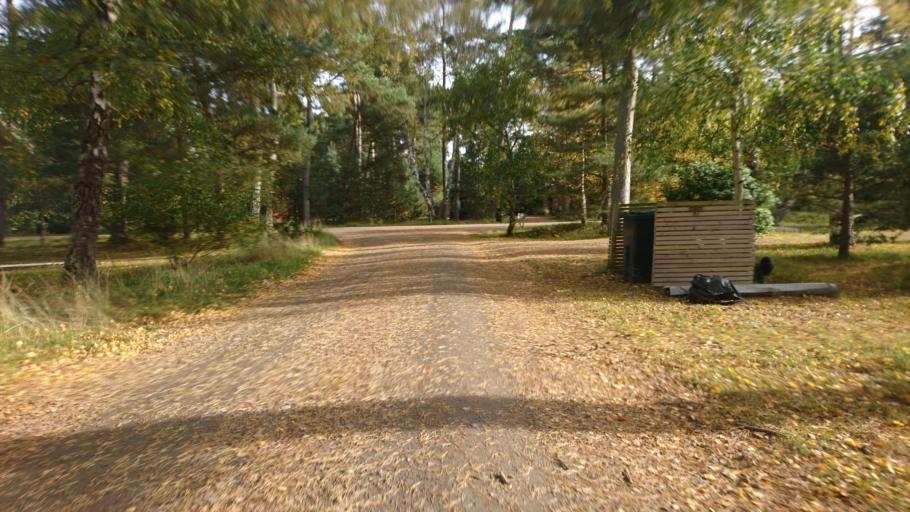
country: SE
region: Skane
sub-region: Vellinge Kommun
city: Ljunghusen
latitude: 55.3973
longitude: 12.9177
